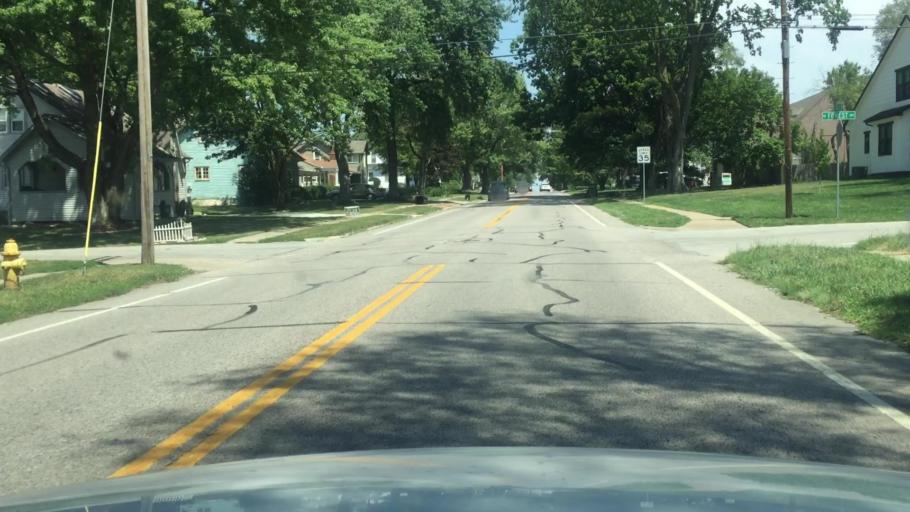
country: US
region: Missouri
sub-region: Jackson County
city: Lees Summit
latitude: 38.9199
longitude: -94.3801
